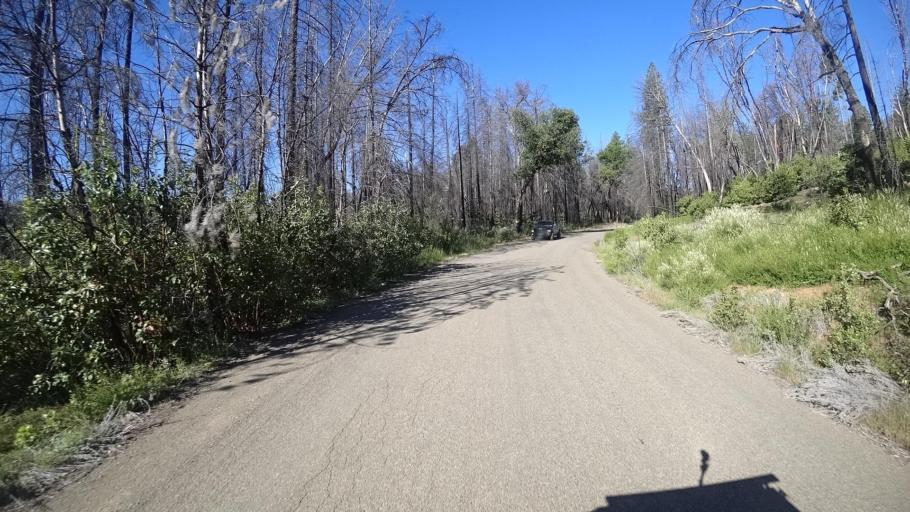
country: US
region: California
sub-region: Lake County
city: Upper Lake
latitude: 39.3952
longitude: -122.9702
